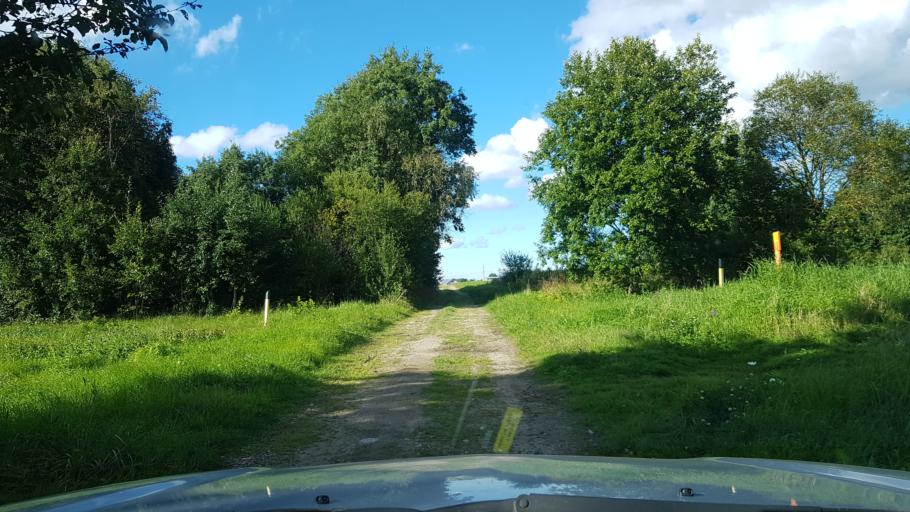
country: EE
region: Harju
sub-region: Kiili vald
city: Kiili
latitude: 59.3591
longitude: 24.8353
